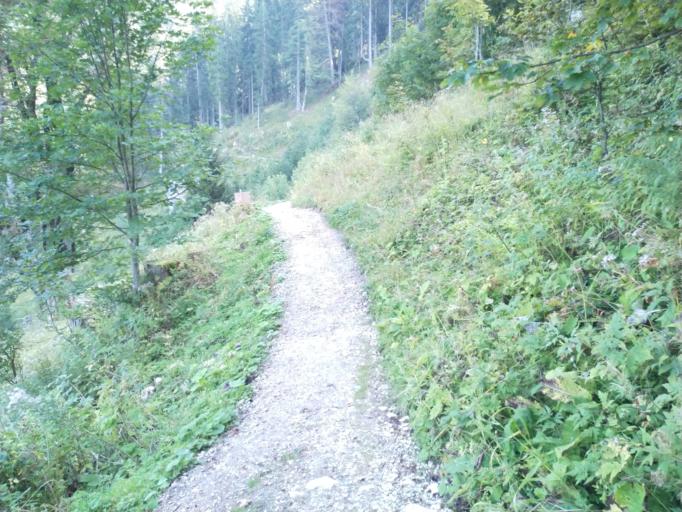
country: DE
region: Bavaria
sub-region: Upper Bavaria
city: Unterammergau
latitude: 47.5883
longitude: 11.0181
